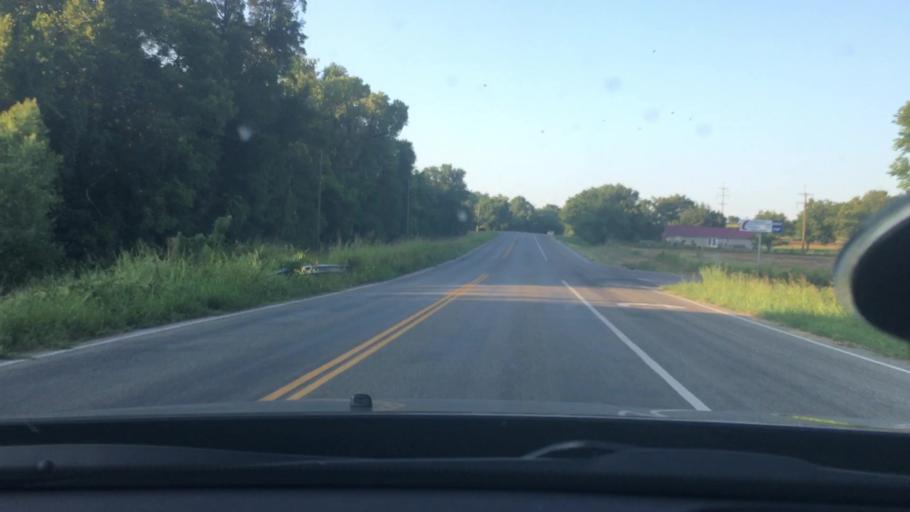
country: US
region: Oklahoma
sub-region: Pontotoc County
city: Byng
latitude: 34.8400
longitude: -96.6786
